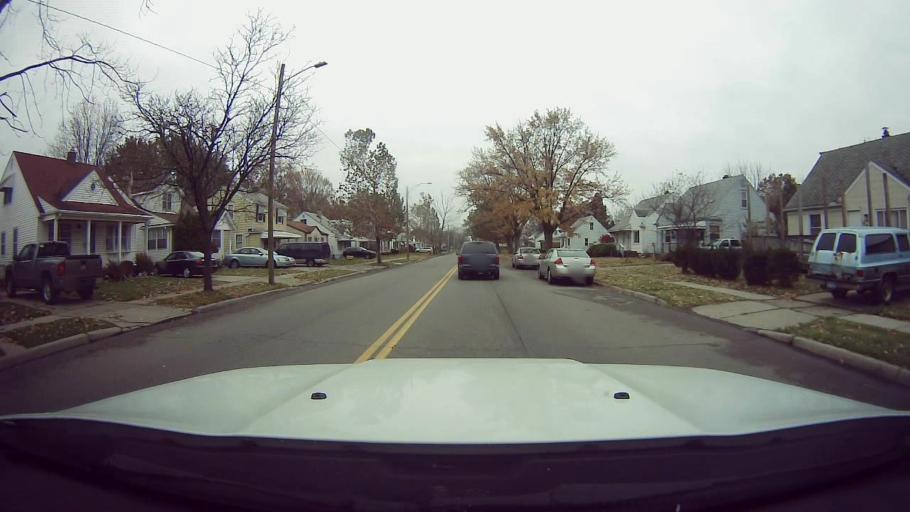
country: US
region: Michigan
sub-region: Wayne County
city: Dearborn Heights
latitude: 42.3385
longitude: -83.2352
